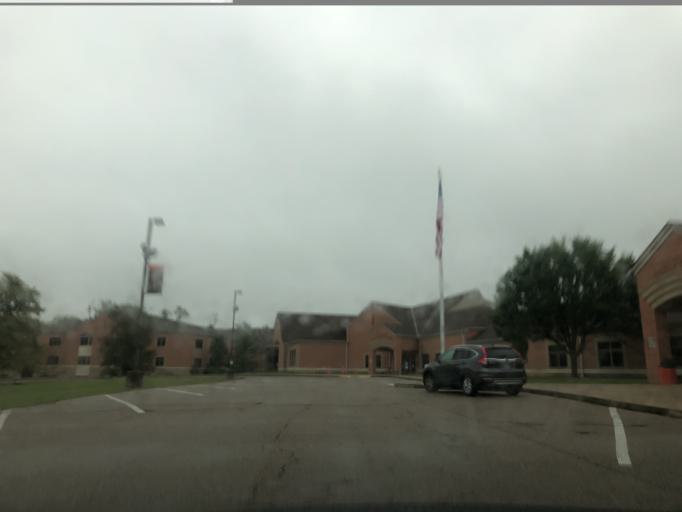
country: US
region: Ohio
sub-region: Hamilton County
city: The Village of Indian Hill
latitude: 39.2626
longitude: -84.2852
